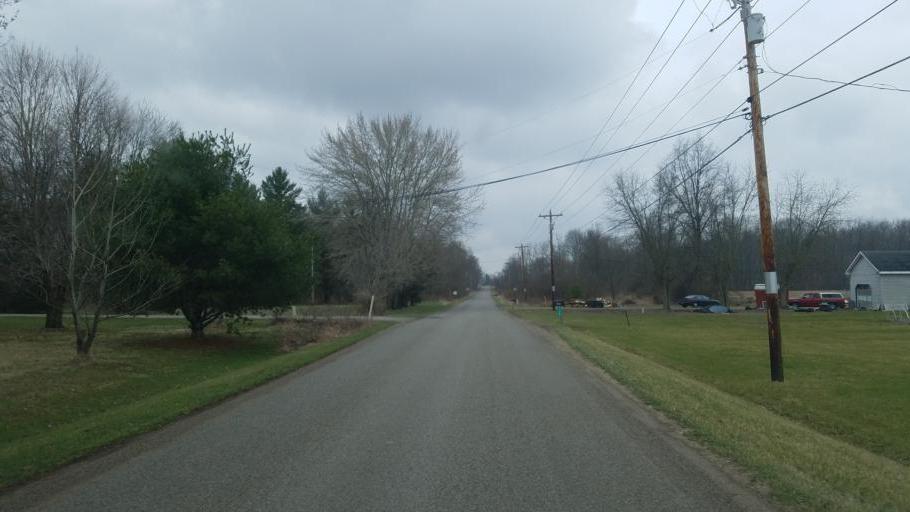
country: US
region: Ohio
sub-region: Delaware County
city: Ashley
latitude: 40.4042
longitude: -82.8524
